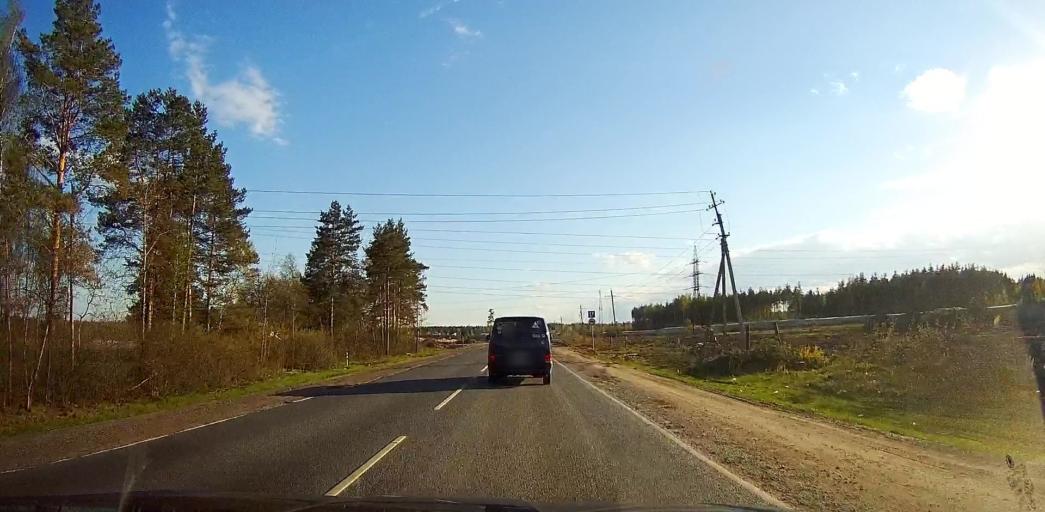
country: RU
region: Moskovskaya
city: Gzhel'
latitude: 55.6368
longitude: 38.3643
